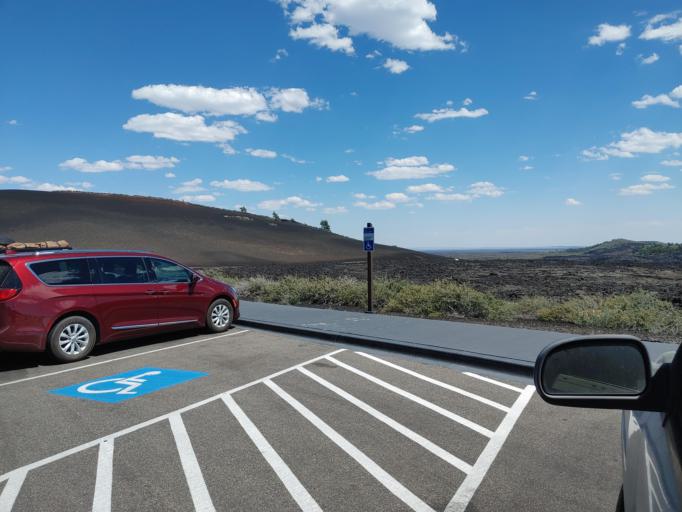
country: US
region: Idaho
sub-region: Butte County
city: Arco
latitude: 43.4417
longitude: -113.5575
